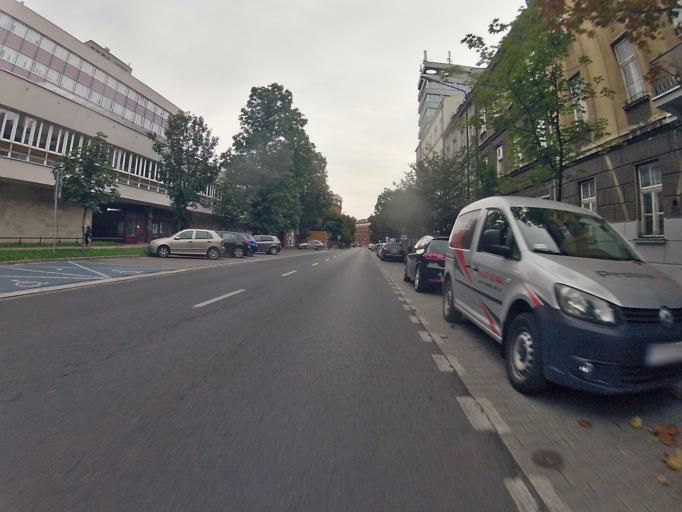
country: PL
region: Lesser Poland Voivodeship
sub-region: Krakow
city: Krakow
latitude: 50.0712
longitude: 19.9403
